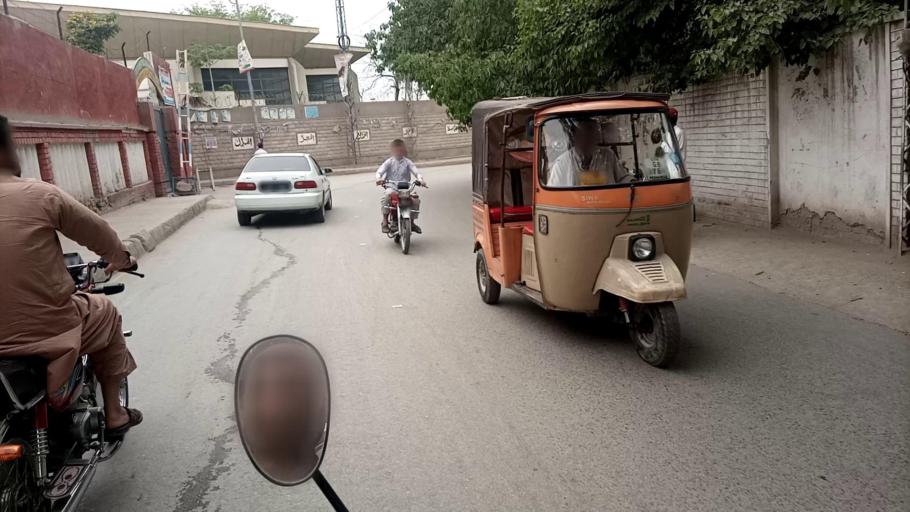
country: PK
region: Khyber Pakhtunkhwa
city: Peshawar
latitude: 33.9934
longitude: 71.5371
